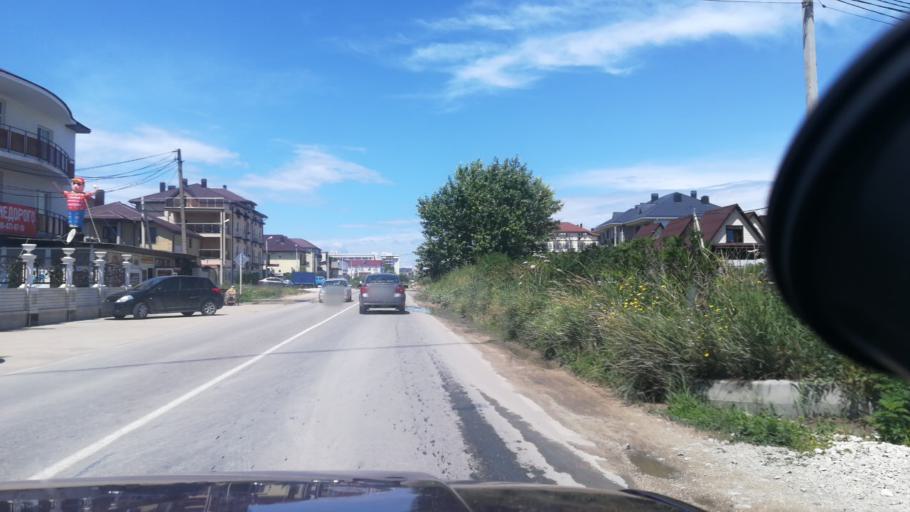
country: RU
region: Krasnodarskiy
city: Vityazevo
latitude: 44.9605
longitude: 37.2949
